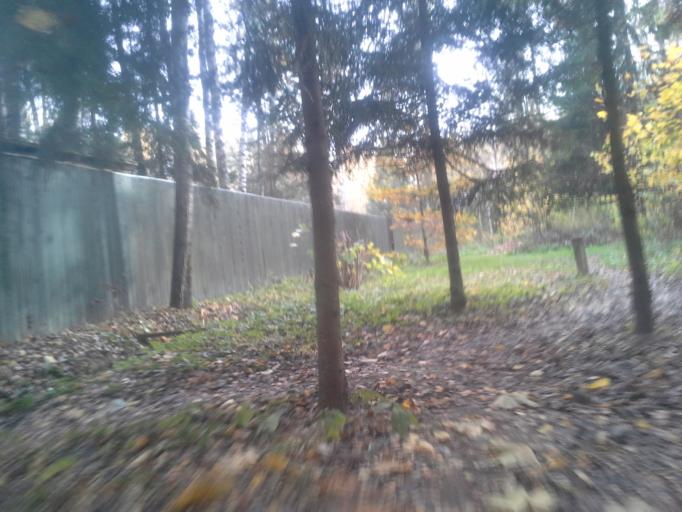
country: RU
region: Moskovskaya
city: Krasnoznamensk
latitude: 55.5810
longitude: 37.0180
